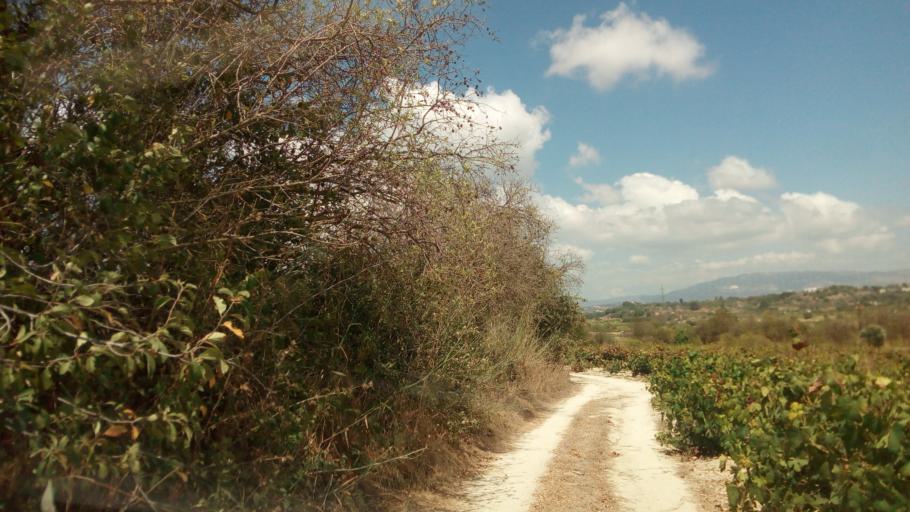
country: CY
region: Pafos
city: Tala
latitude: 34.8847
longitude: 32.4857
